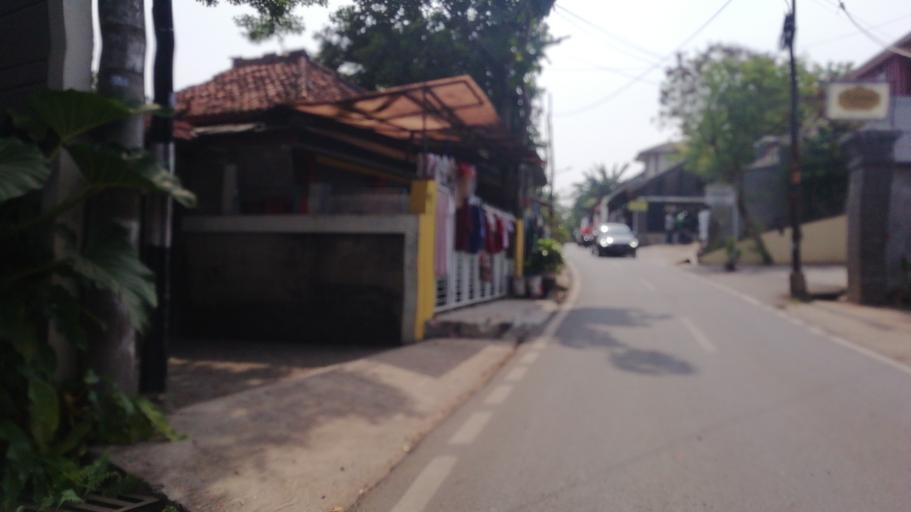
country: ID
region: West Java
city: Depok
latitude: -6.3511
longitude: 106.7968
